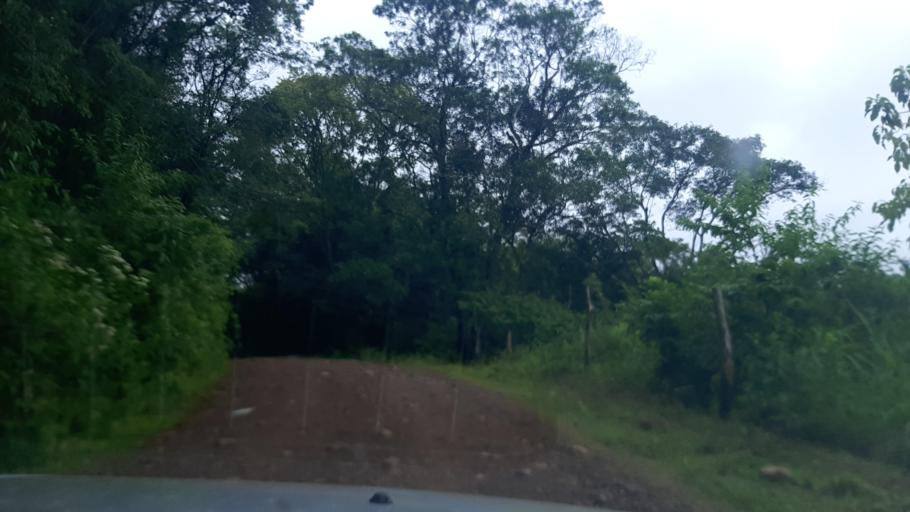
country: BR
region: Parana
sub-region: Ampere
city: Ampere
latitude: -26.0584
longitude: -53.5493
